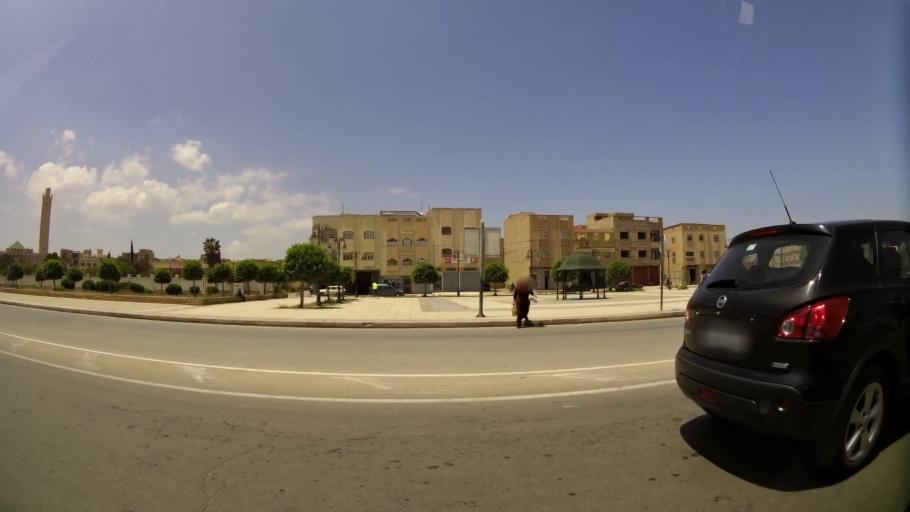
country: MA
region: Oriental
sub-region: Oujda-Angad
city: Oujda
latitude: 34.7011
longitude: -1.8974
